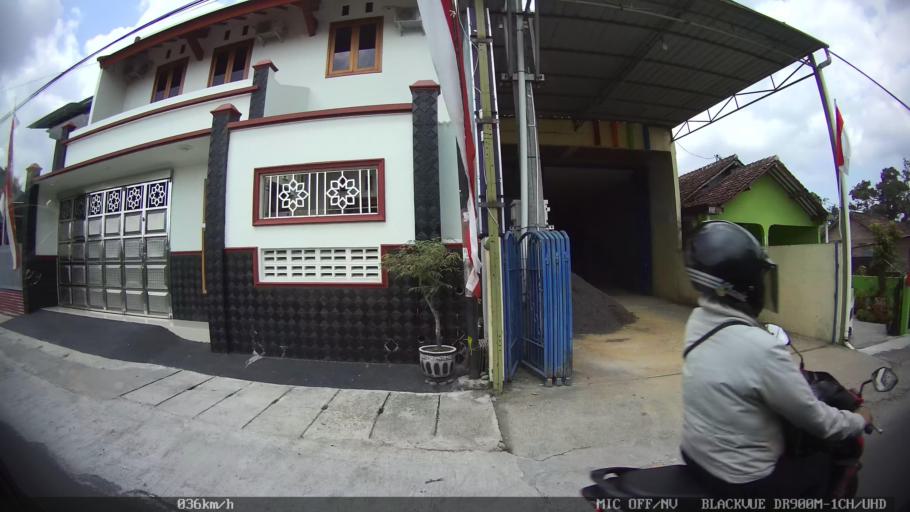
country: ID
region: Daerah Istimewa Yogyakarta
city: Gamping Lor
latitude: -7.8027
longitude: 110.3332
